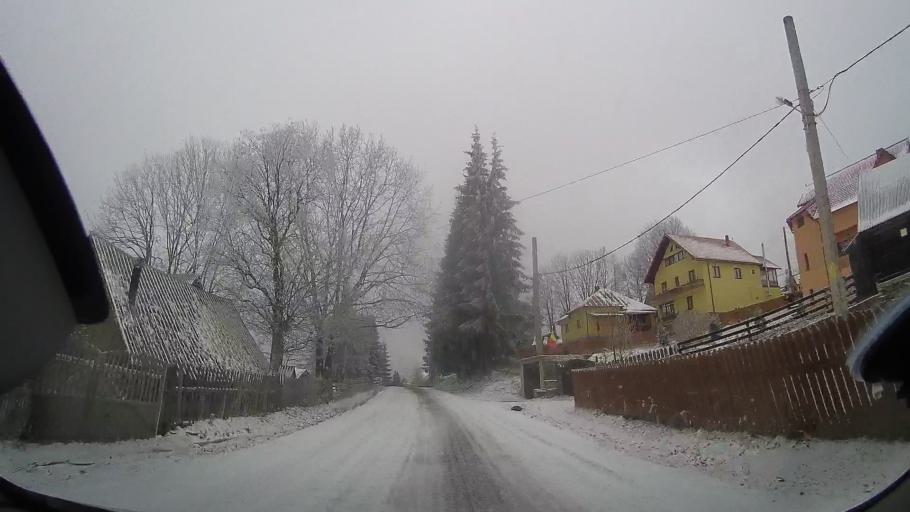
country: RO
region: Cluj
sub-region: Comuna Maguri-Racatau
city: Maguri
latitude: 46.6487
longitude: 23.0778
